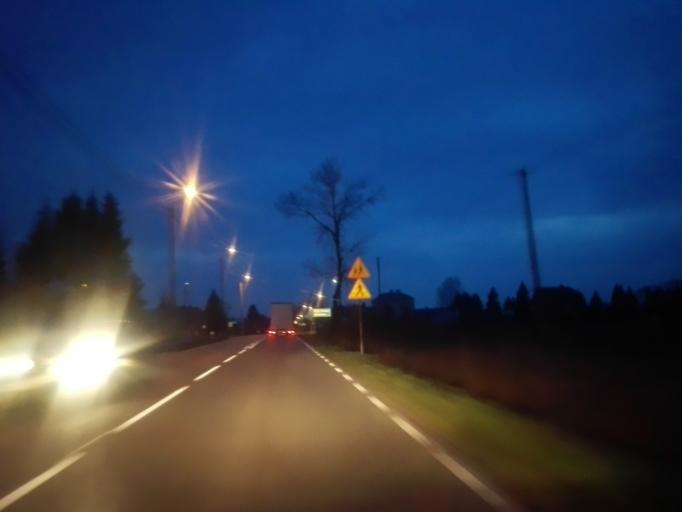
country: PL
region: Podlasie
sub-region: Powiat lomzynski
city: Sniadowo
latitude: 53.0405
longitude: 21.9871
